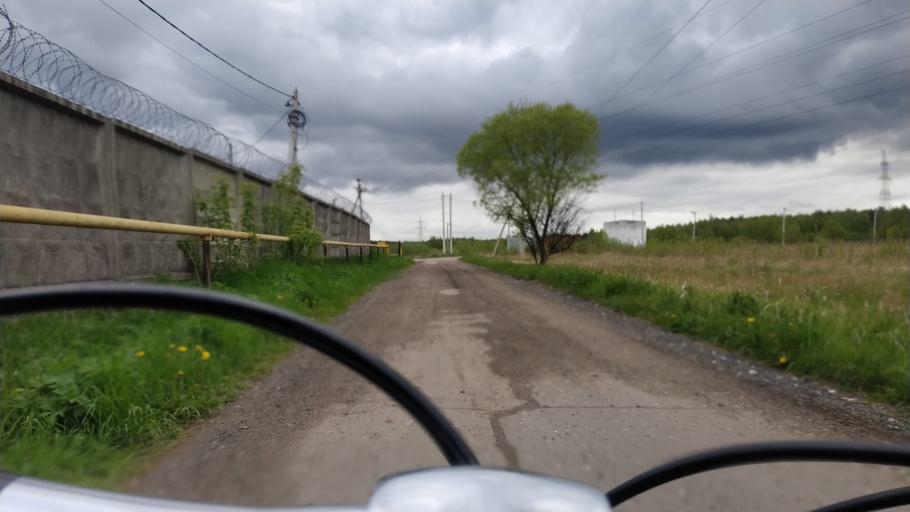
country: RU
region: Moskovskaya
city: Rechitsy
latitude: 55.6184
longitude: 38.5344
